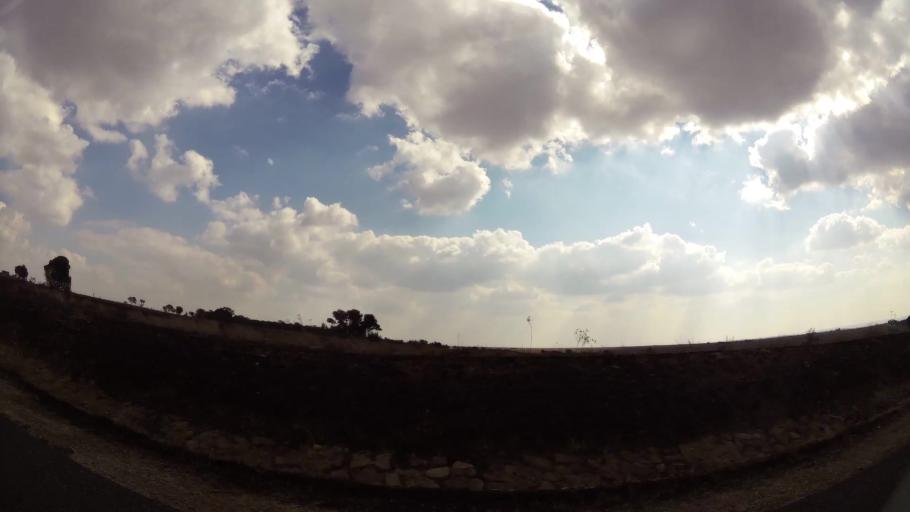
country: ZA
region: Mpumalanga
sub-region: Nkangala District Municipality
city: Delmas
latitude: -26.0919
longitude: 28.6757
